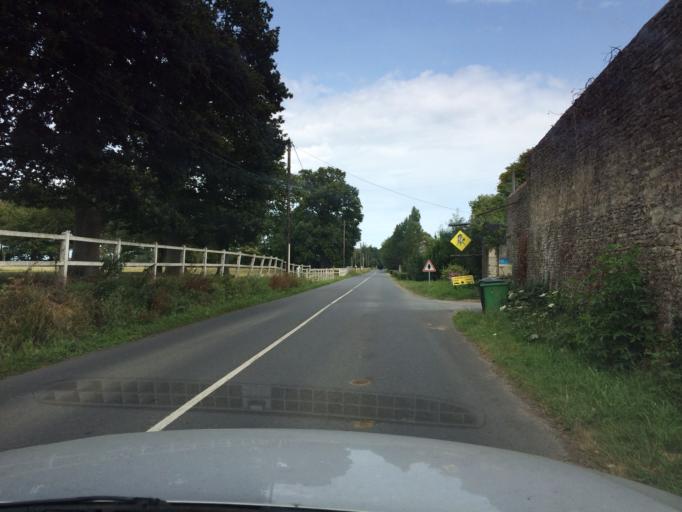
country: FR
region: Lower Normandy
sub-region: Departement du Calvados
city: Saint-Vigor-le-Grand
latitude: 49.3261
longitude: -0.6480
